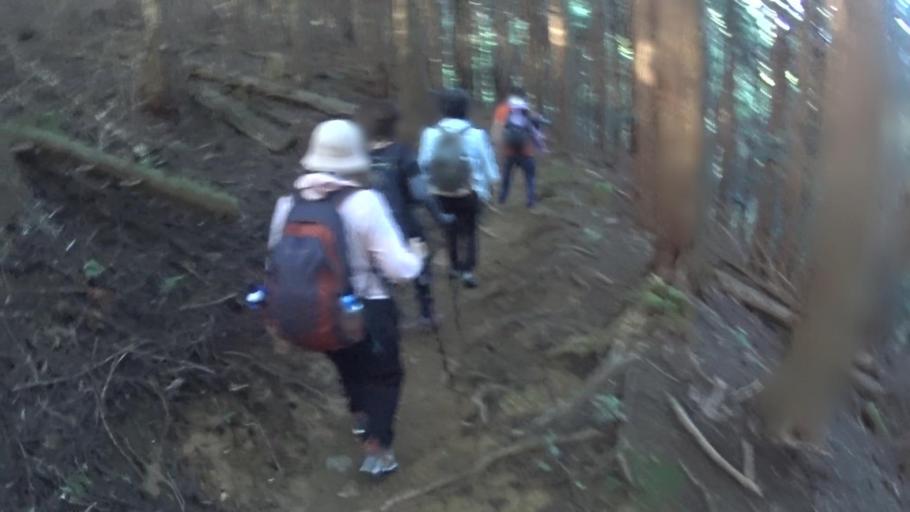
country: JP
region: Shiga Prefecture
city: Kitahama
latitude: 35.1047
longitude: 135.8440
